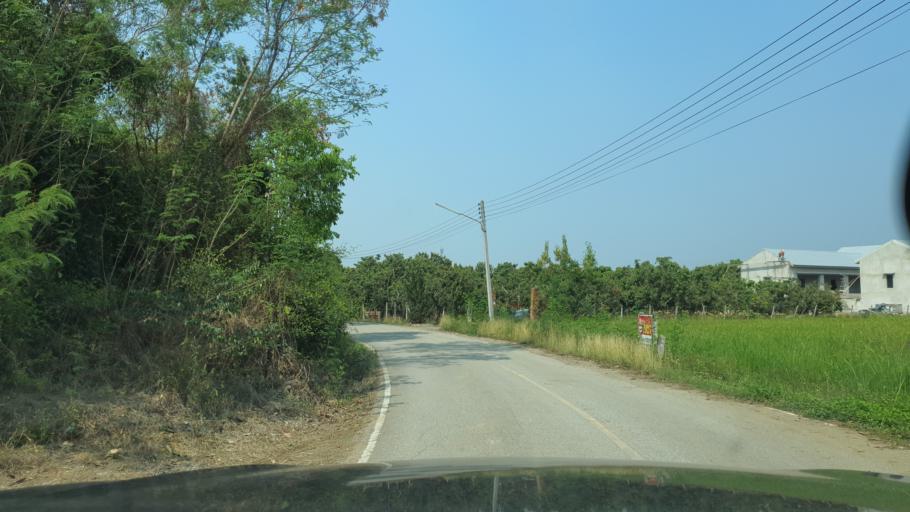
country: TH
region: Chiang Mai
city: Saraphi
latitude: 18.7321
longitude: 99.0694
